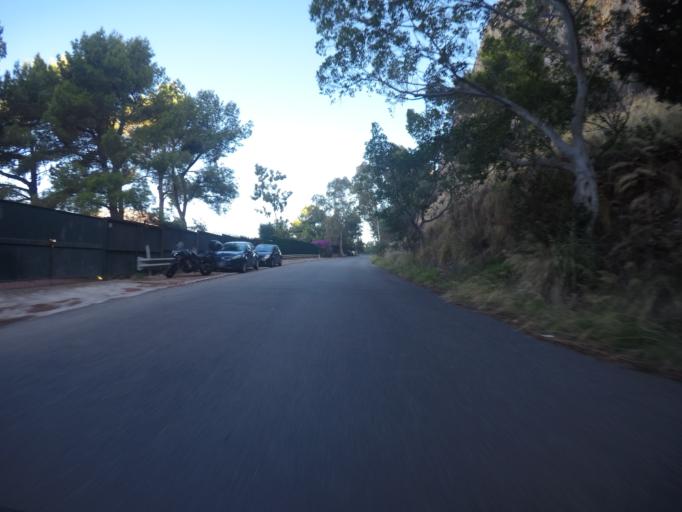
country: IT
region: Sicily
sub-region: Palermo
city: Palermo
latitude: 38.1929
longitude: 13.3374
